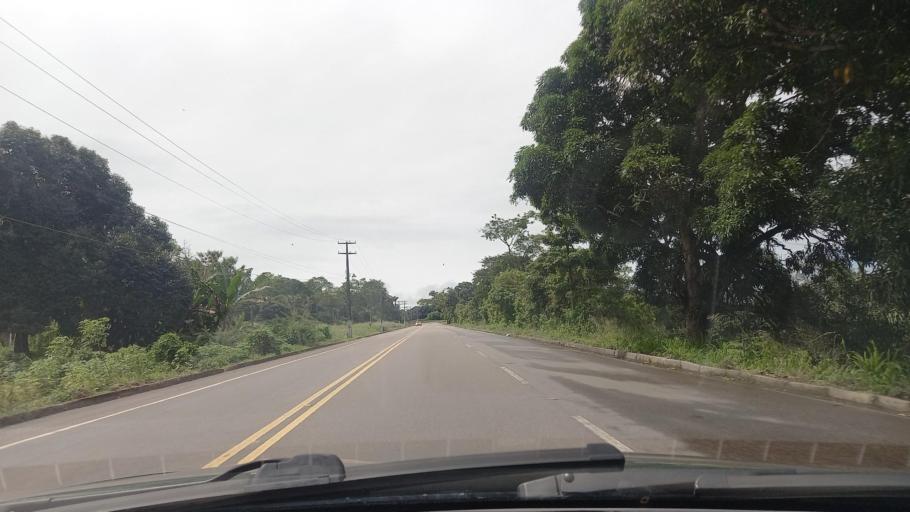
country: BR
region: Alagoas
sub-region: Sao Miguel Dos Campos
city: Sao Miguel dos Campos
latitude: -9.8090
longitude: -36.2166
